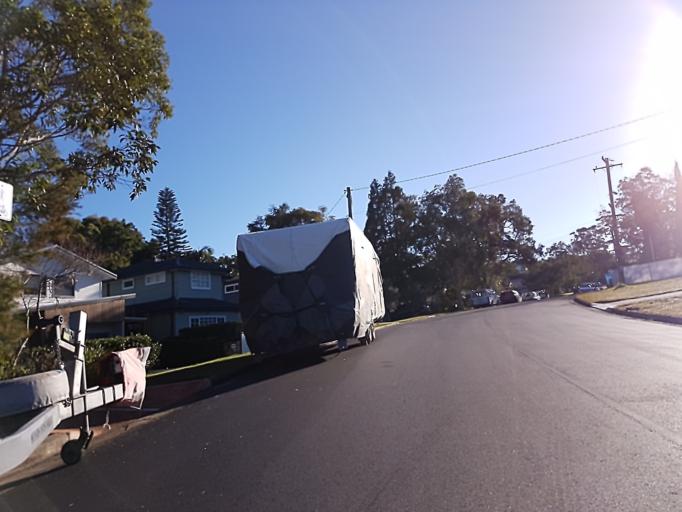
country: AU
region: New South Wales
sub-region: Manly Vale
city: Balgowlah
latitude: -33.7893
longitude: 151.2476
